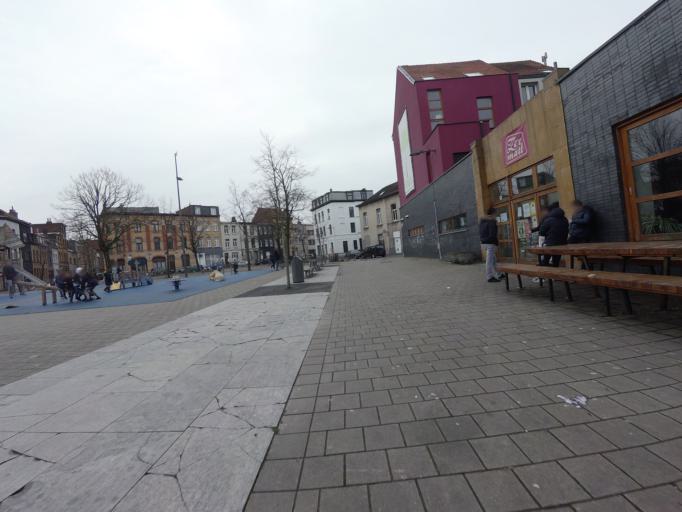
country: BE
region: Flanders
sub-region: Provincie Antwerpen
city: Antwerpen
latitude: 51.2195
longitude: 4.4438
